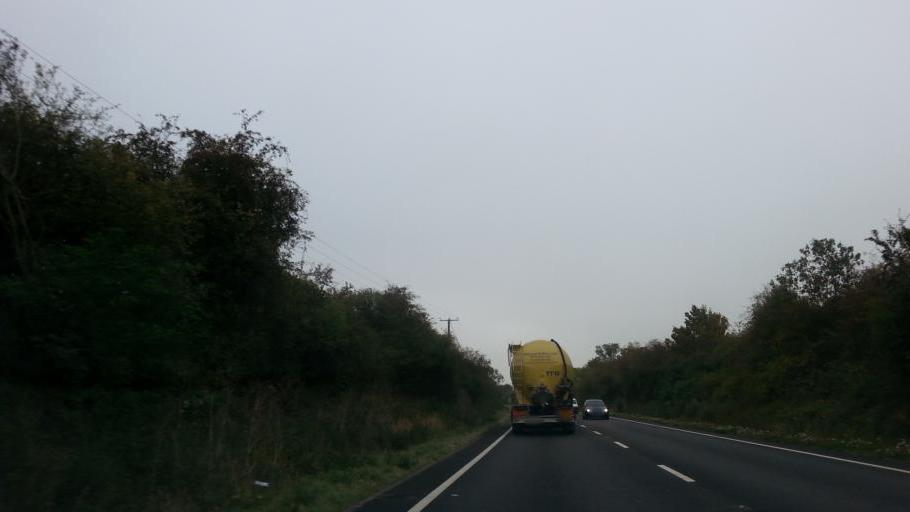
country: GB
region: England
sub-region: Northamptonshire
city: Oundle
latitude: 52.4619
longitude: -0.4617
